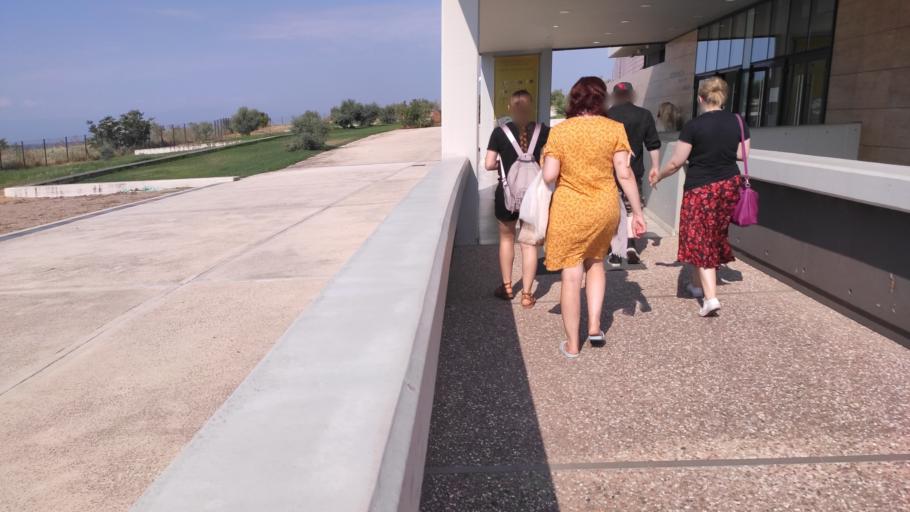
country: GR
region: Central Macedonia
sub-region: Nomos Pellis
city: Pella
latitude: 40.7618
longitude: 22.5197
